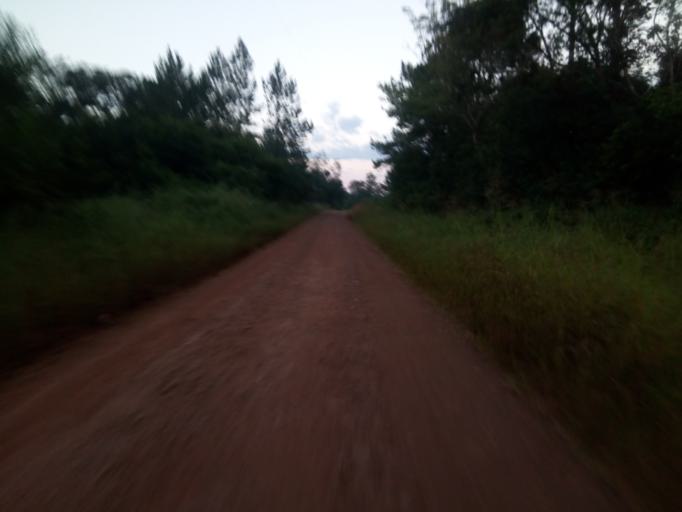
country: AR
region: Misiones
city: Almafuerte
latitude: -27.5638
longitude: -55.4098
